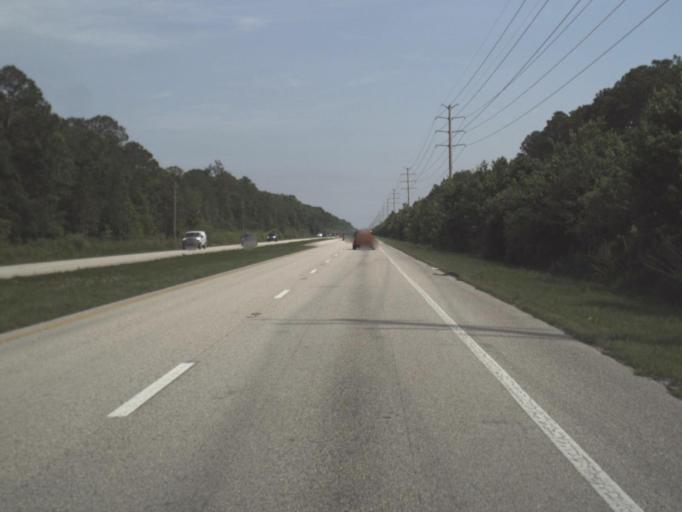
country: US
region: Florida
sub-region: Saint Johns County
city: Palm Valley
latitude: 30.0625
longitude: -81.4372
